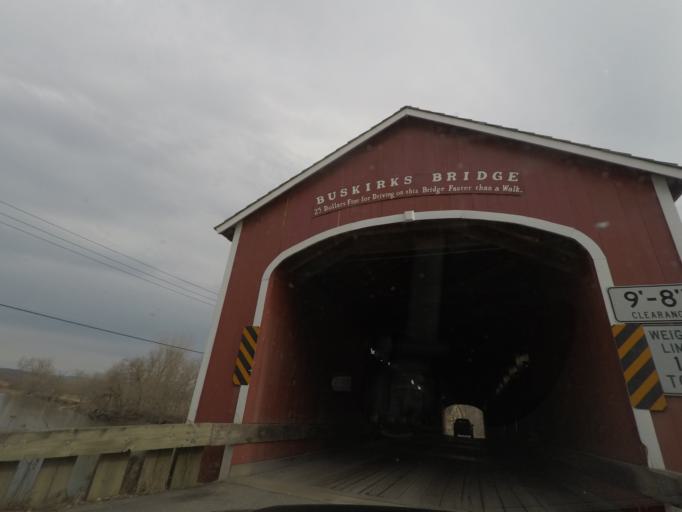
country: US
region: New York
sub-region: Washington County
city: Cambridge
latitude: 42.9585
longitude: -73.4333
